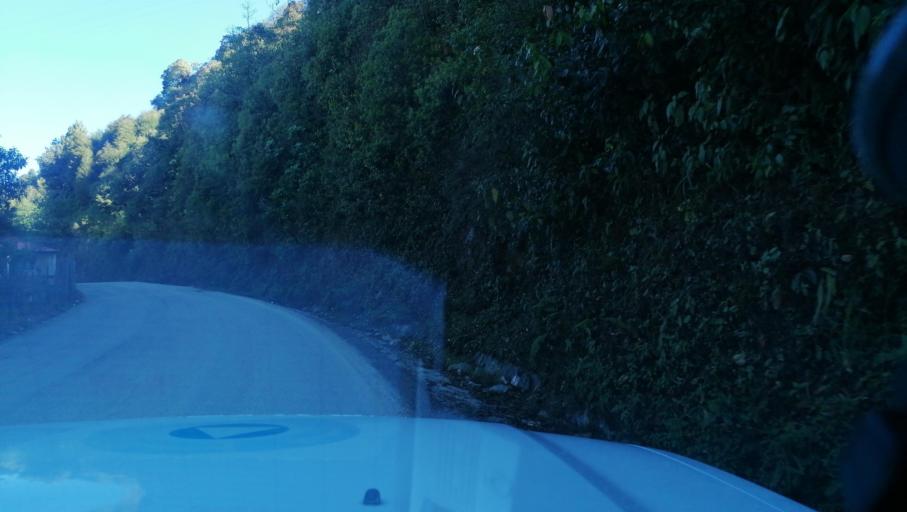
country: MX
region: Chiapas
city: Motozintla de Mendoza
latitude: 15.2679
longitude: -92.2273
